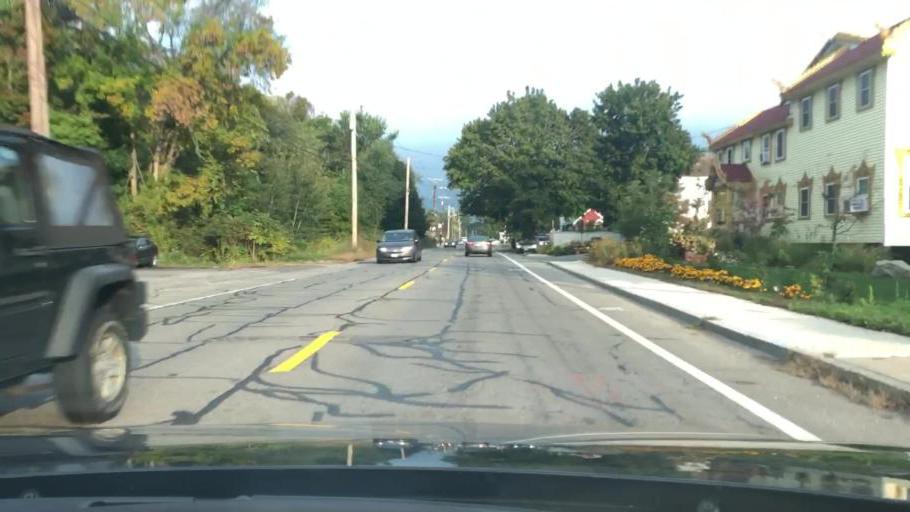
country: US
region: Massachusetts
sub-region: Middlesex County
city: Tyngsboro
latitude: 42.6434
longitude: -71.3896
